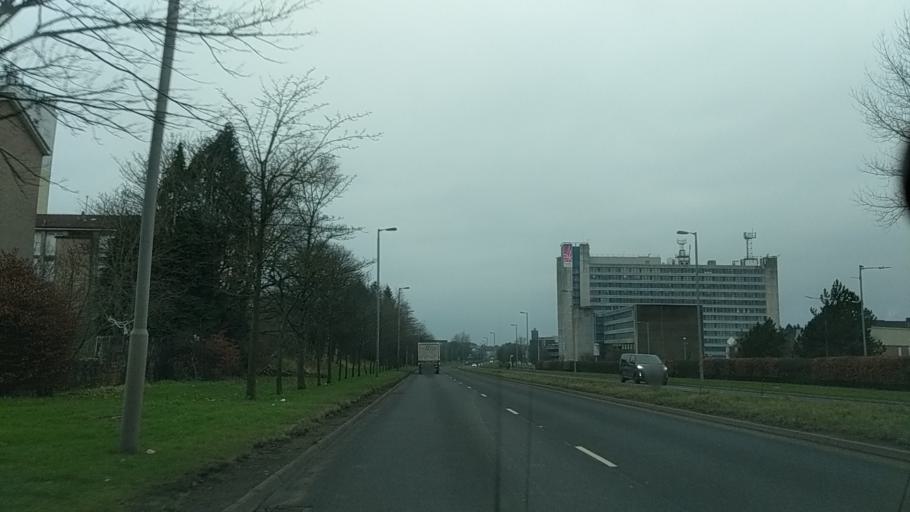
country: GB
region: Scotland
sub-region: South Lanarkshire
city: East Kilbride
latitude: 55.7586
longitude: -4.1754
